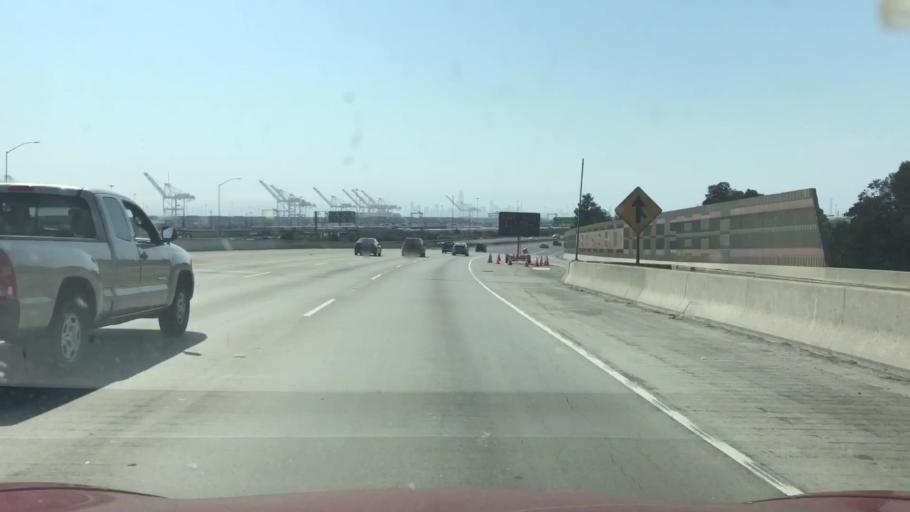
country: US
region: California
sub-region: Alameda County
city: Oakland
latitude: 37.8035
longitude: -122.2928
